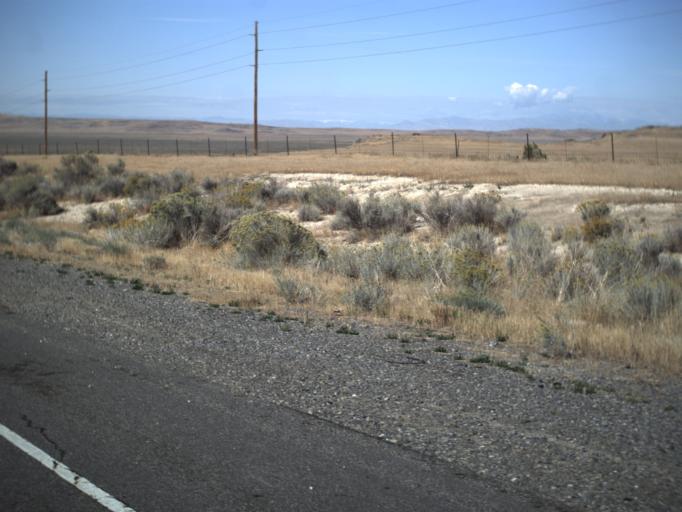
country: US
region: Utah
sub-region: Tooele County
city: Grantsville
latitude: 40.7599
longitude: -113.0141
